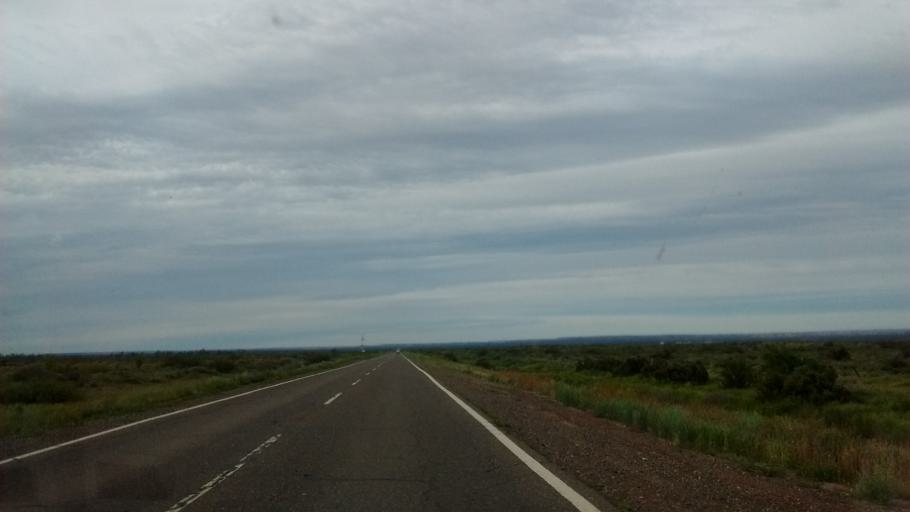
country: AR
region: Rio Negro
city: Catriel
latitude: -38.0126
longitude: -67.9135
